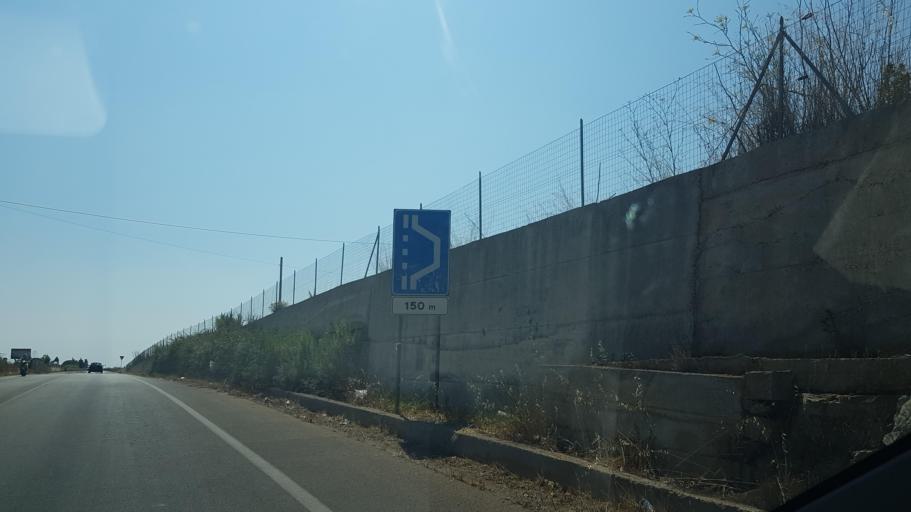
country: IT
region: Apulia
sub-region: Provincia di Lecce
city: Taurisano
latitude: 39.9494
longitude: 18.1971
